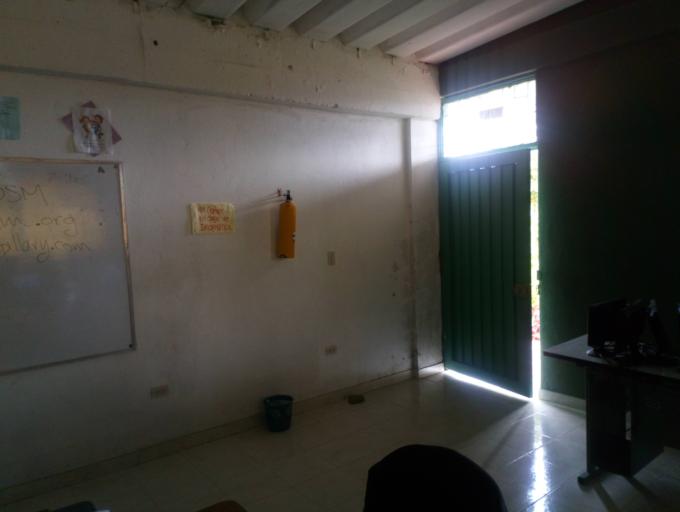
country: CO
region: Boyaca
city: Soata
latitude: 6.3318
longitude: -72.6863
